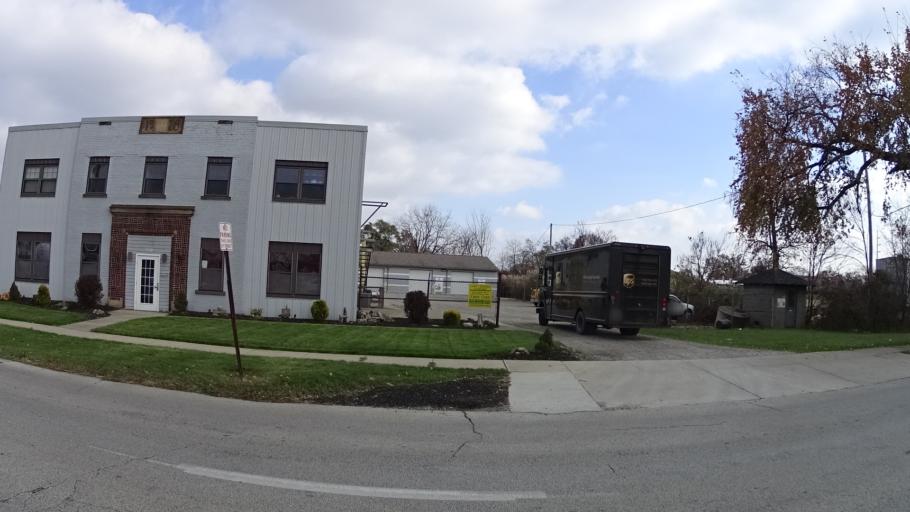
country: US
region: Ohio
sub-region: Lorain County
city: Elyria
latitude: 41.3729
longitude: -82.0859
